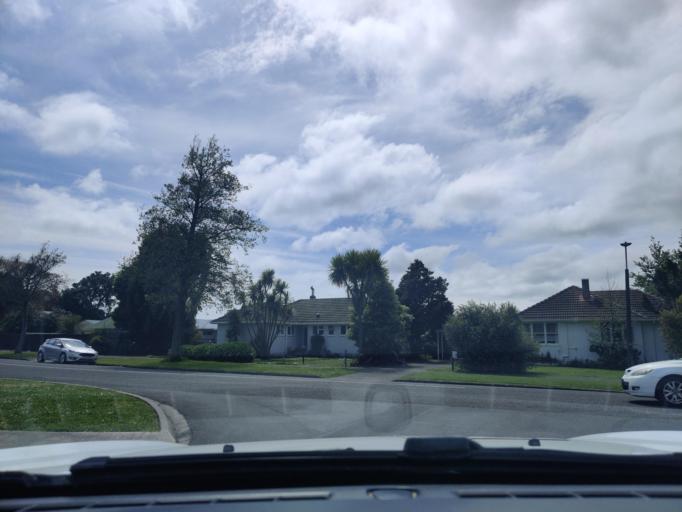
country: NZ
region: Manawatu-Wanganui
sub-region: Palmerston North City
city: Palmerston North
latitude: -40.3498
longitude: 175.5904
